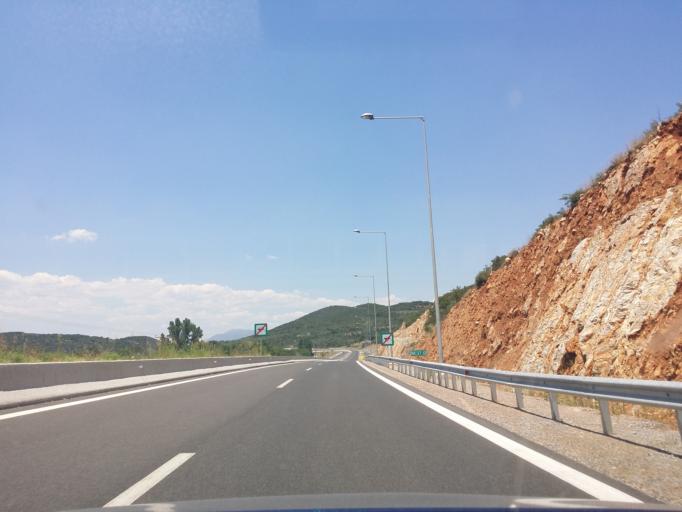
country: GR
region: Peloponnese
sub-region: Nomos Lakonias
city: Magoula
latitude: 37.1520
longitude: 22.3848
